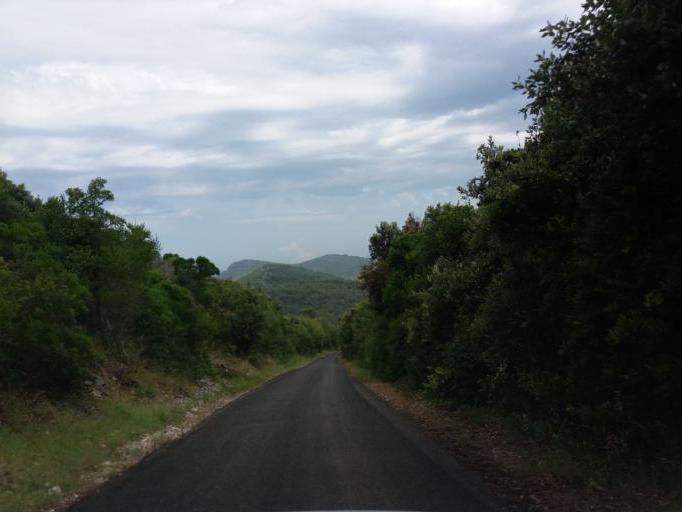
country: HR
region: Zadarska
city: Sali
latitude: 43.9078
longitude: 15.1308
